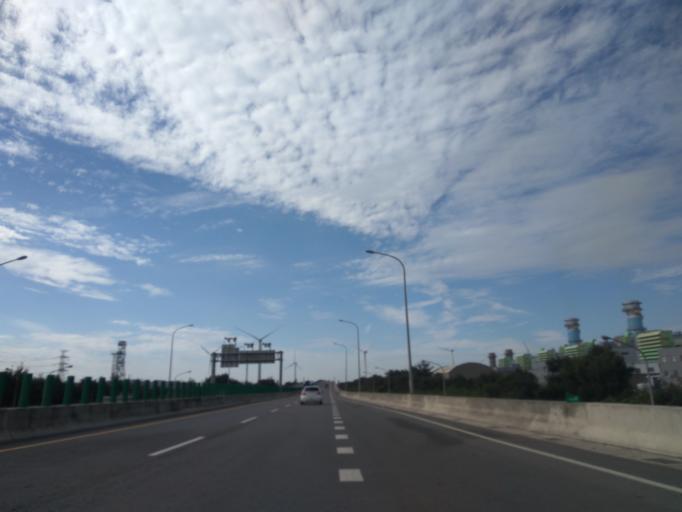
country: TW
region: Taiwan
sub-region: Hsinchu
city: Zhubei
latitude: 25.0262
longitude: 121.0498
